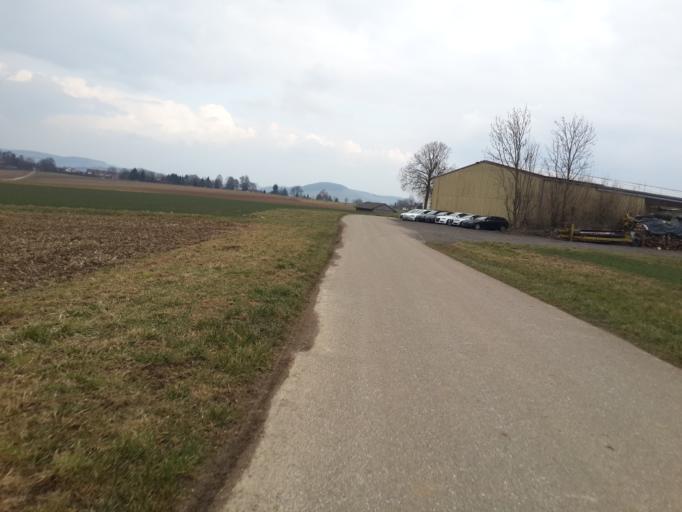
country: DE
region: Baden-Wuerttemberg
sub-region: Regierungsbezirk Stuttgart
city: Untereisesheim
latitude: 49.1727
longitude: 9.1818
